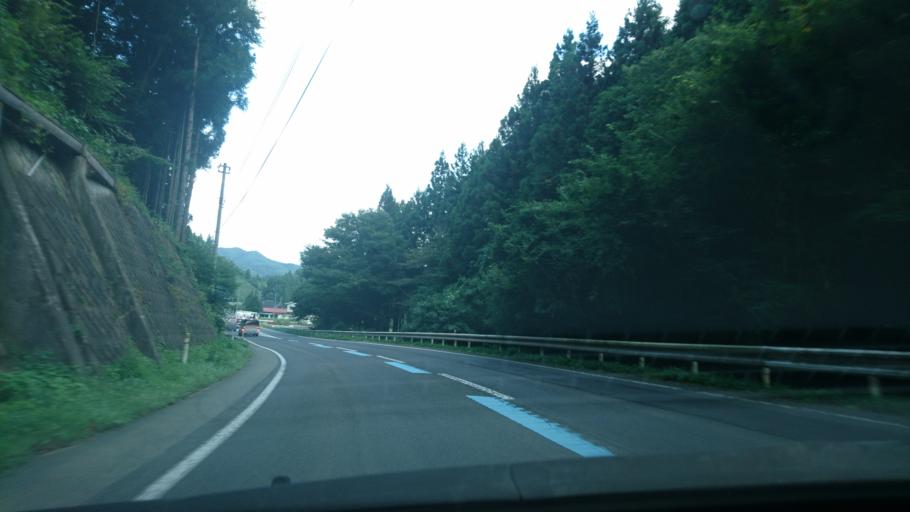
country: JP
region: Iwate
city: Mizusawa
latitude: 39.0412
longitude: 141.2437
